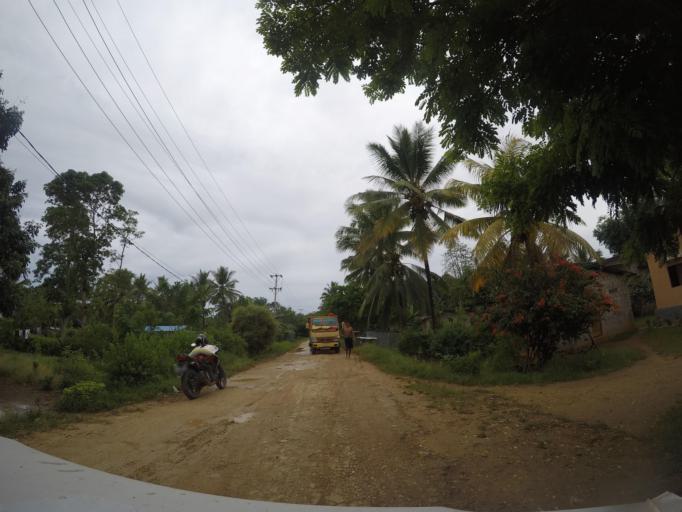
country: TL
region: Lautem
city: Lospalos
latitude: -8.5340
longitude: 126.9971
